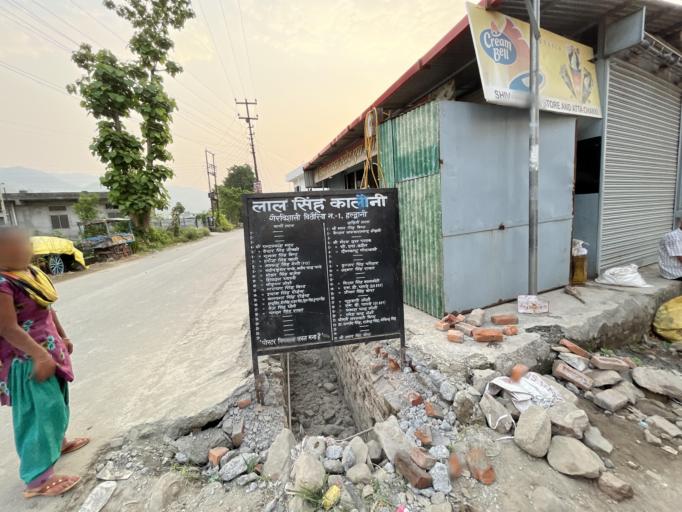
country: IN
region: Uttarakhand
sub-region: Naini Tal
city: Haldwani
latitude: 29.2327
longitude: 79.5077
